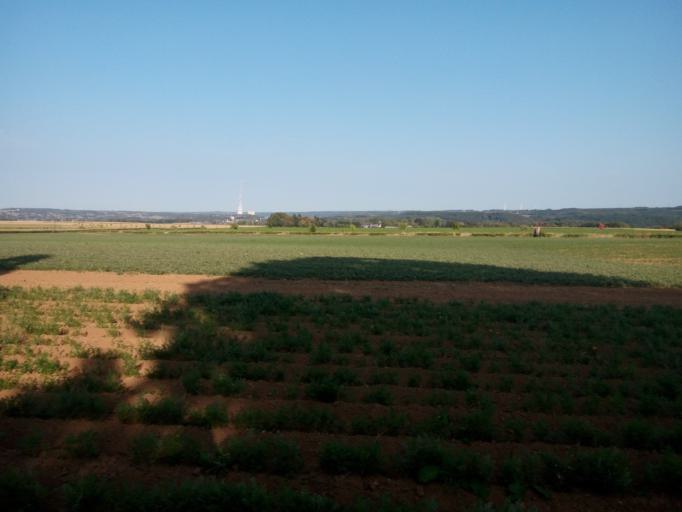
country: BE
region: Wallonia
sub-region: Province de Liege
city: Heron
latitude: 50.5258
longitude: 5.1506
